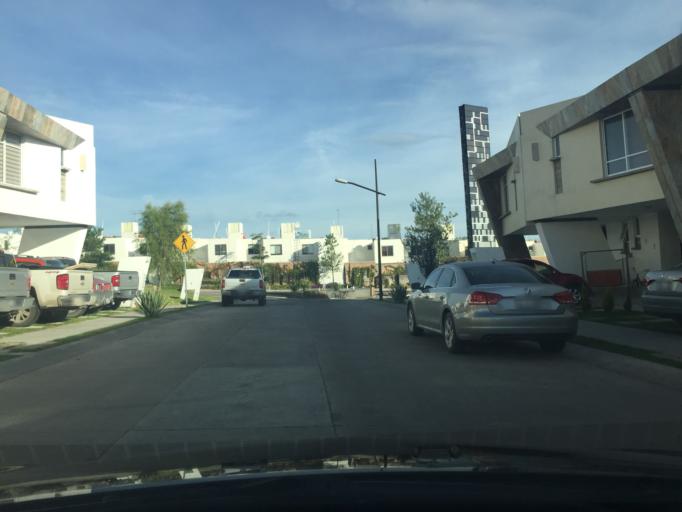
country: MX
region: Guanajuato
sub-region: Leon
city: La Ermita
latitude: 21.1689
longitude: -101.7351
